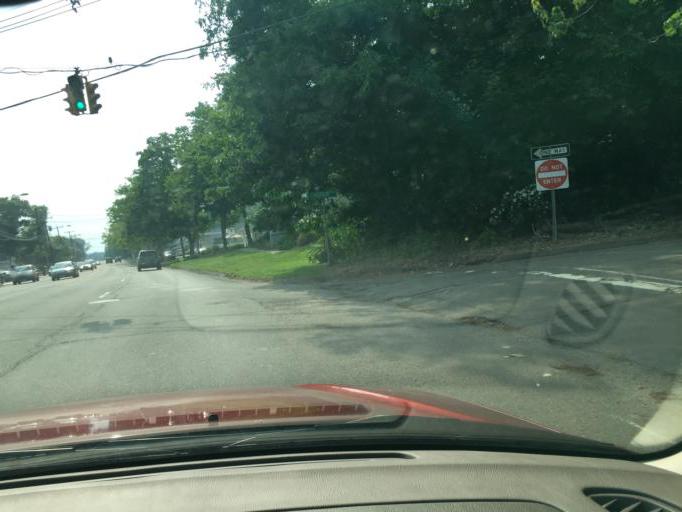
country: US
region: Connecticut
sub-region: Fairfield County
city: Westport
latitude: 41.1391
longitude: -73.3276
